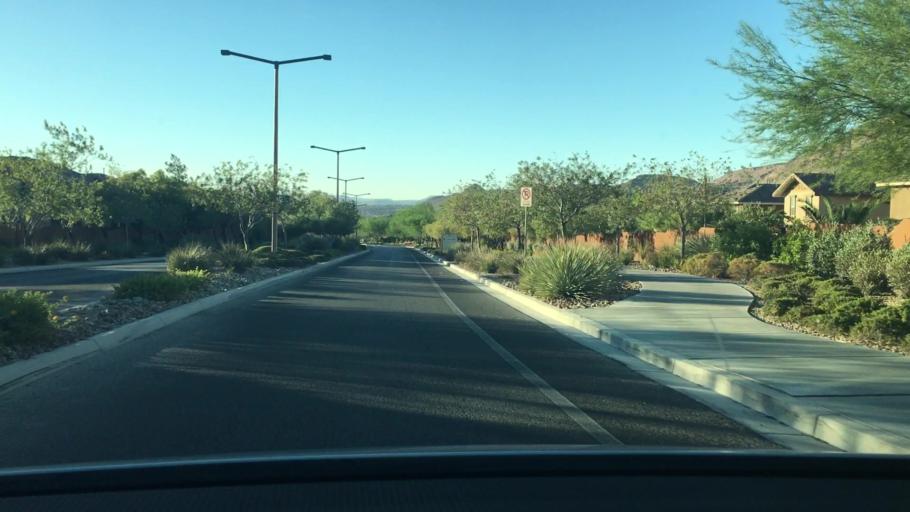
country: US
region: Nevada
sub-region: Clark County
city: Summerlin South
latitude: 36.0895
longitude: -115.3245
